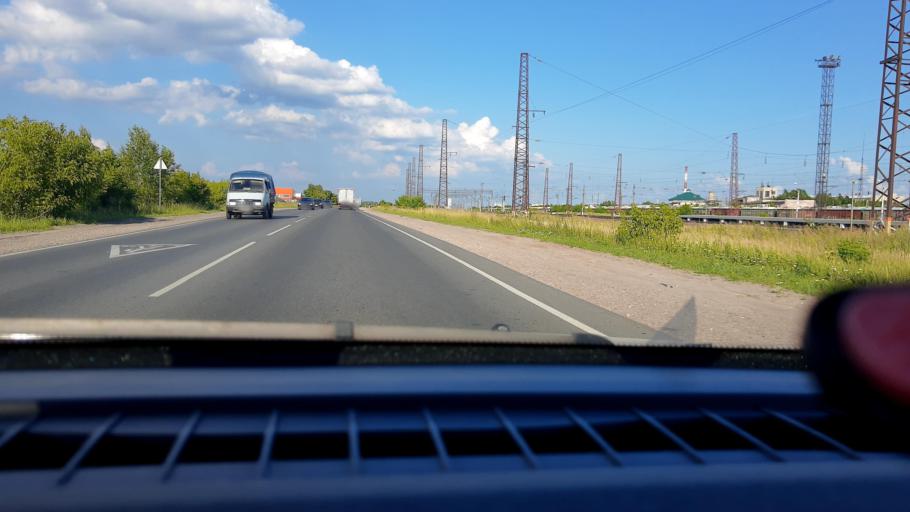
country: RU
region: Nizjnij Novgorod
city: Babino
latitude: 56.2529
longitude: 43.5810
